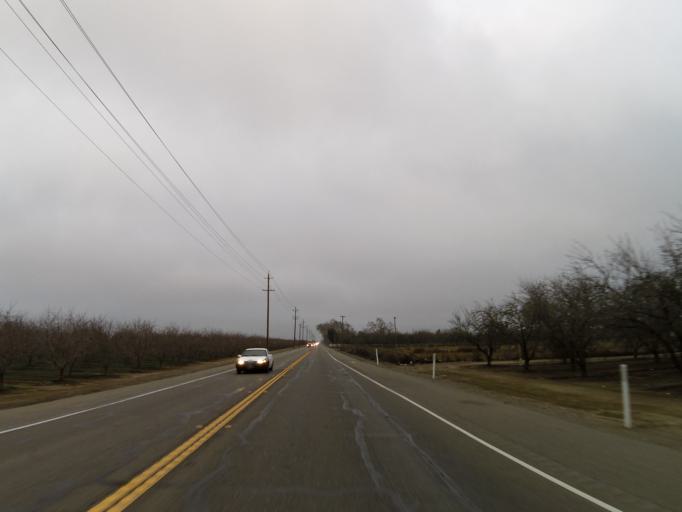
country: US
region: California
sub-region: Stanislaus County
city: Riverdale Park
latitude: 37.6382
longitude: -121.0720
